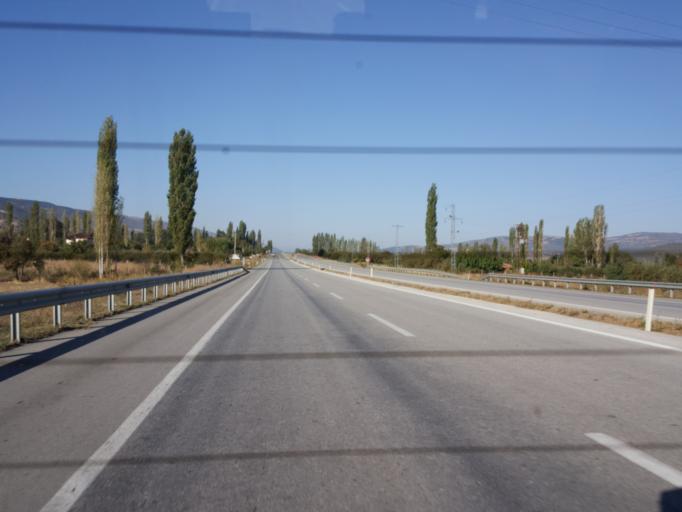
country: TR
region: Amasya
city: Ezinepazari
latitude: 40.5720
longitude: 36.1136
